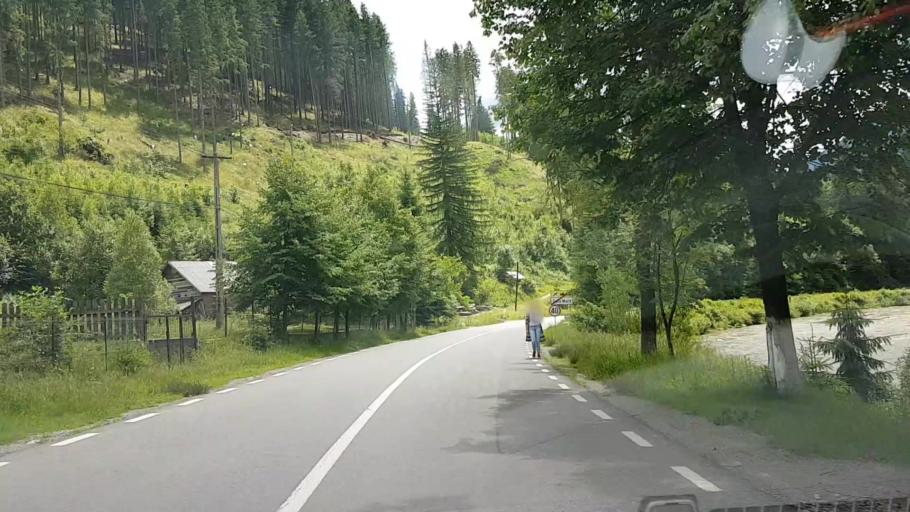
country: RO
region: Suceava
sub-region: Comuna Crucea
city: Crucea
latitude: 47.3546
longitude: 25.6154
